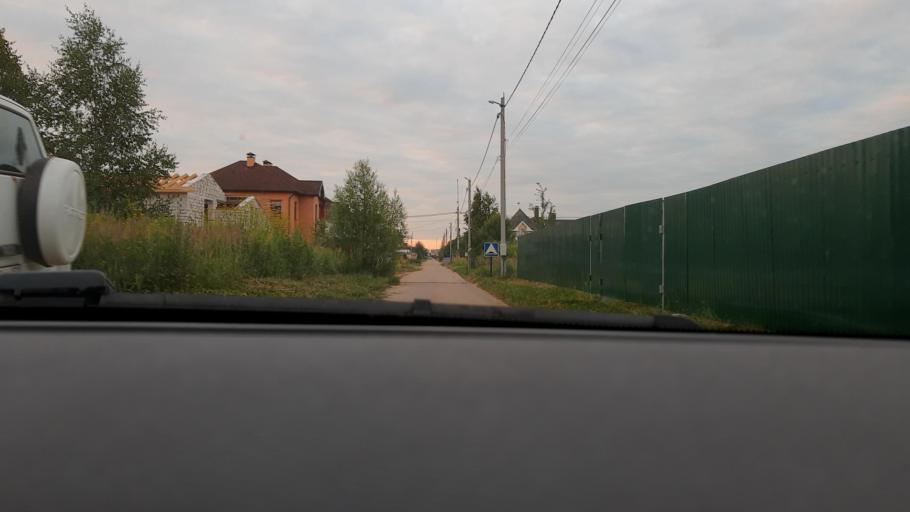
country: RU
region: Nizjnij Novgorod
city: Burevestnik
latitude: 56.1947
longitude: 43.8631
